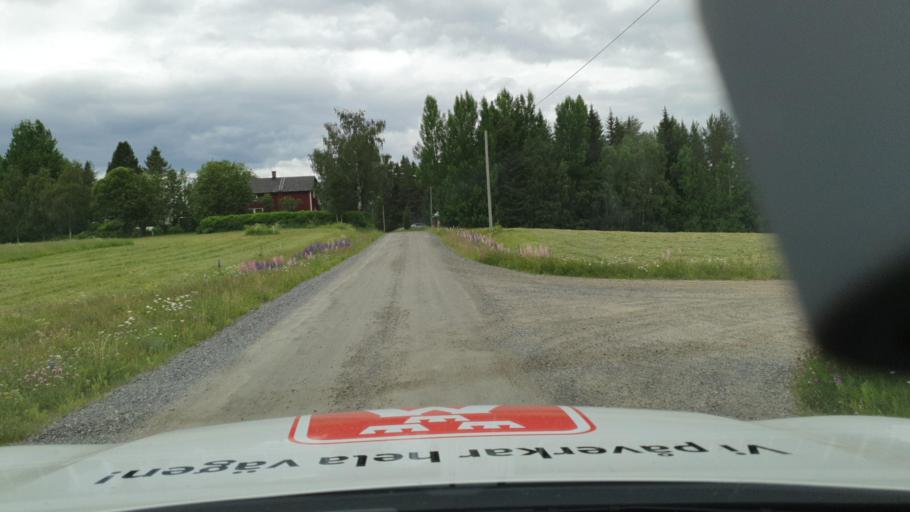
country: SE
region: Vaesterbotten
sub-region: Bjurholms Kommun
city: Bjurholm
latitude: 63.7395
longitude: 19.2867
